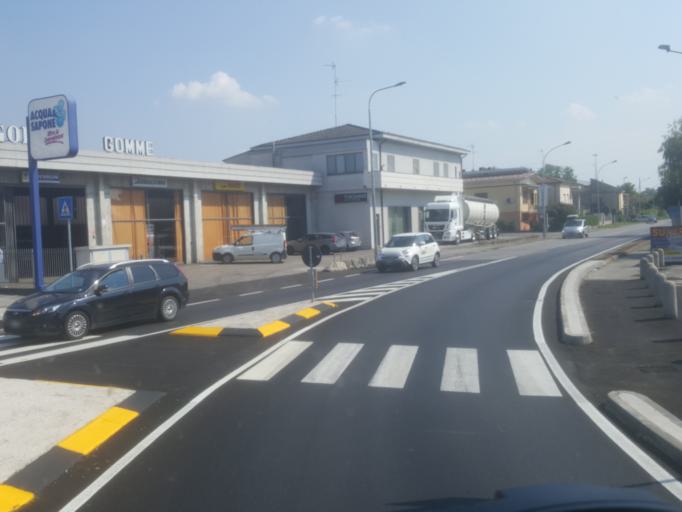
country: IT
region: Lombardy
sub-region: Provincia di Cremona
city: Casalmaggiore
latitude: 44.9837
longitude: 10.4224
